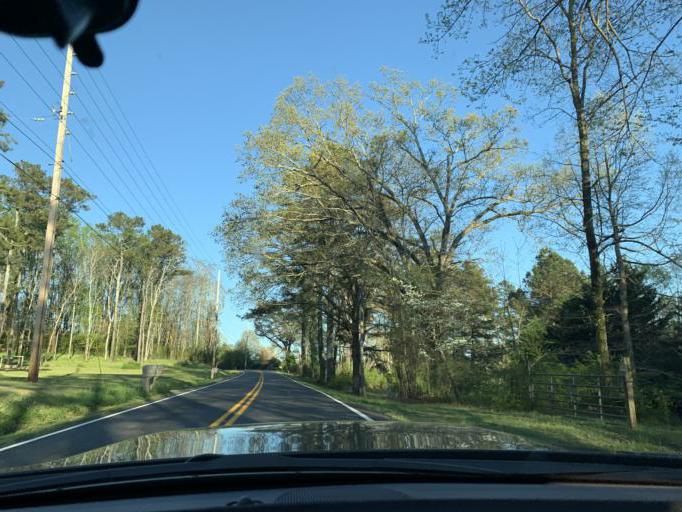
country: US
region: Georgia
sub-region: Forsyth County
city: Cumming
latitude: 34.2570
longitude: -84.2026
